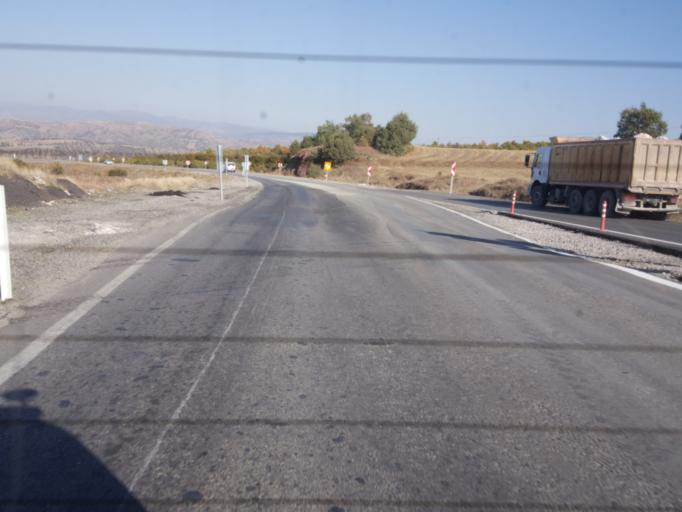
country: TR
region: Corum
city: Seydim
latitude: 40.5881
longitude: 34.7503
